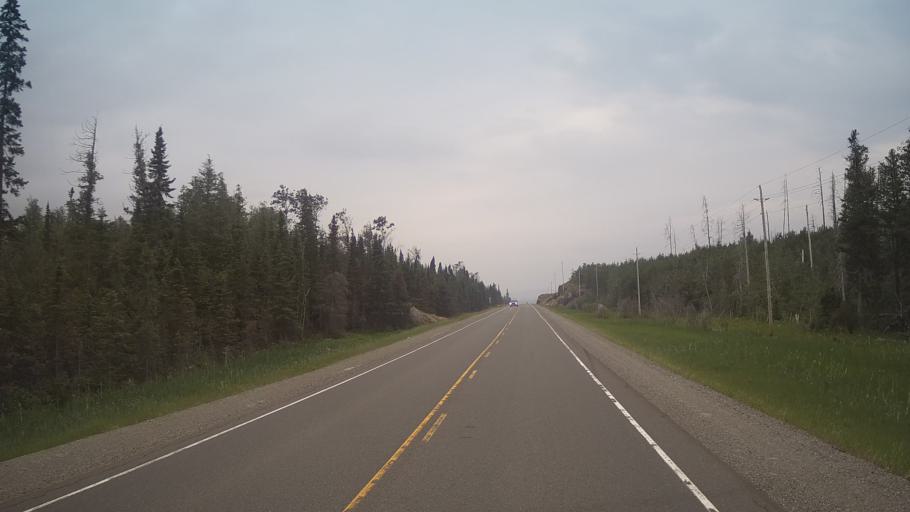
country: CA
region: Ontario
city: Greenstone
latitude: 49.5143
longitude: -88.0356
